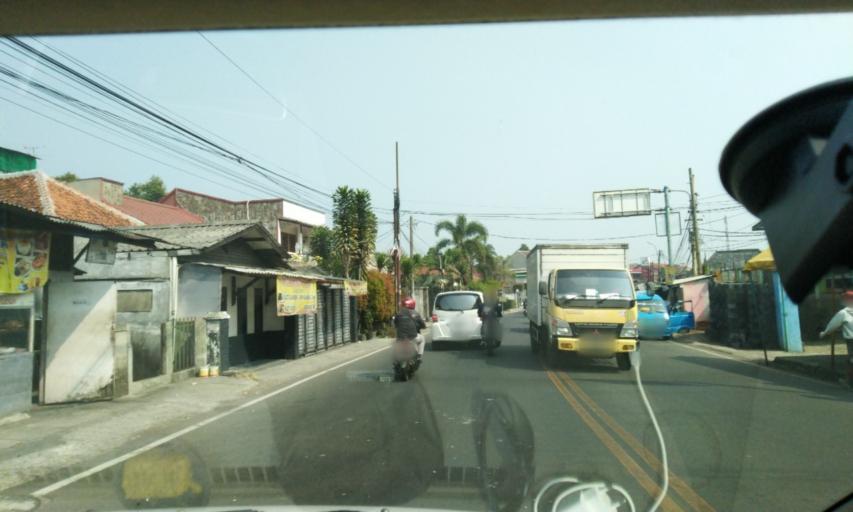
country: ID
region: West Java
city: Caringin
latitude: -6.6632
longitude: 106.8554
